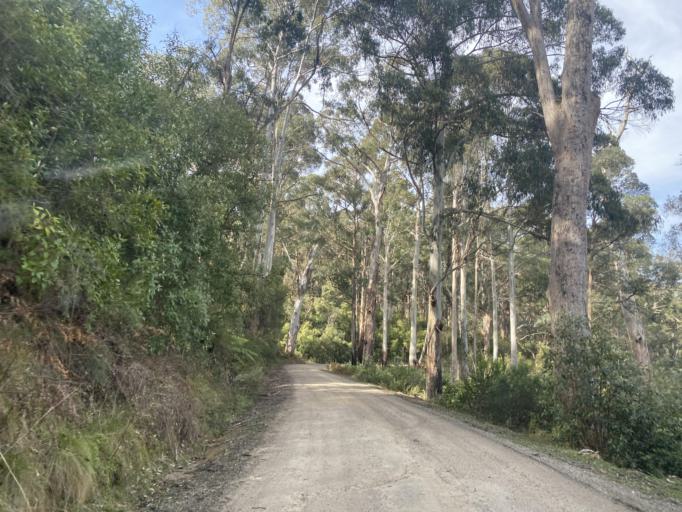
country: AU
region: Victoria
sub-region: Mansfield
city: Mansfield
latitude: -36.8441
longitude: 146.1723
